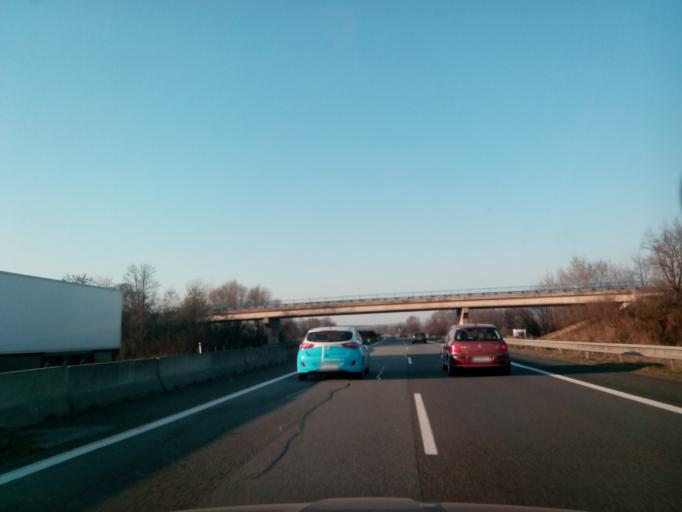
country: SK
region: Kosicky
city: Kosice
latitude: 48.8145
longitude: 21.3101
